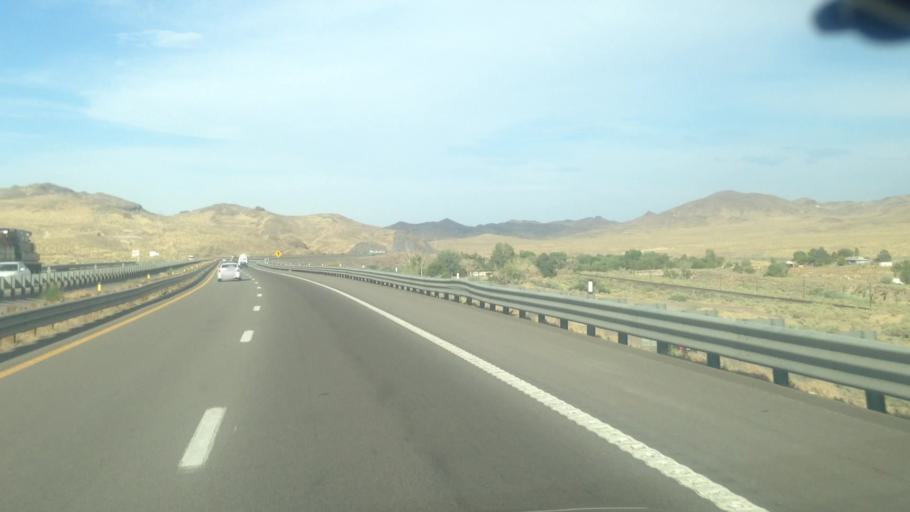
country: US
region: Nevada
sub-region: Lyon County
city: Fernley
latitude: 39.5892
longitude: -119.3922
